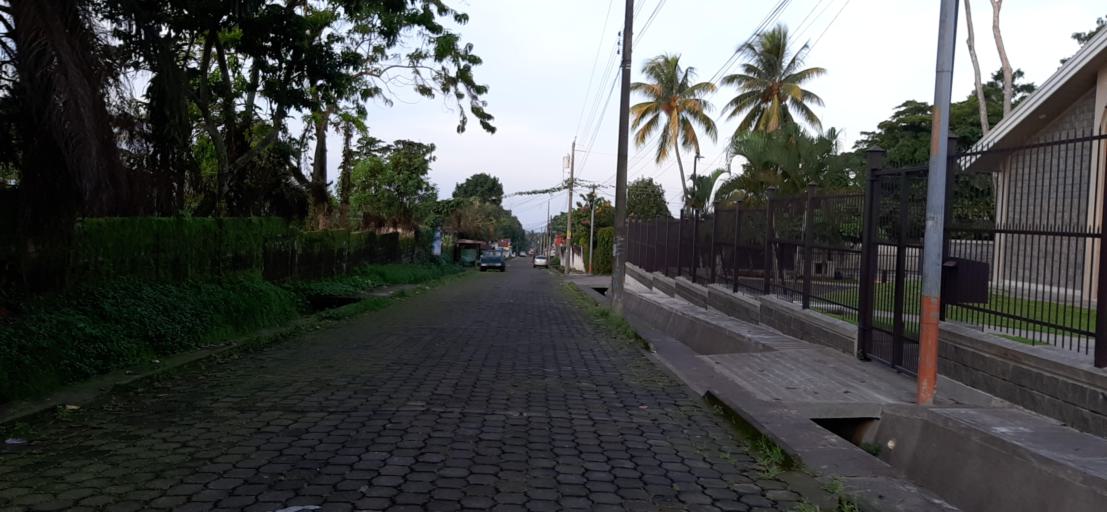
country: GT
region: Retalhuleu
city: San Felipe
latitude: 14.6233
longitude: -91.6010
